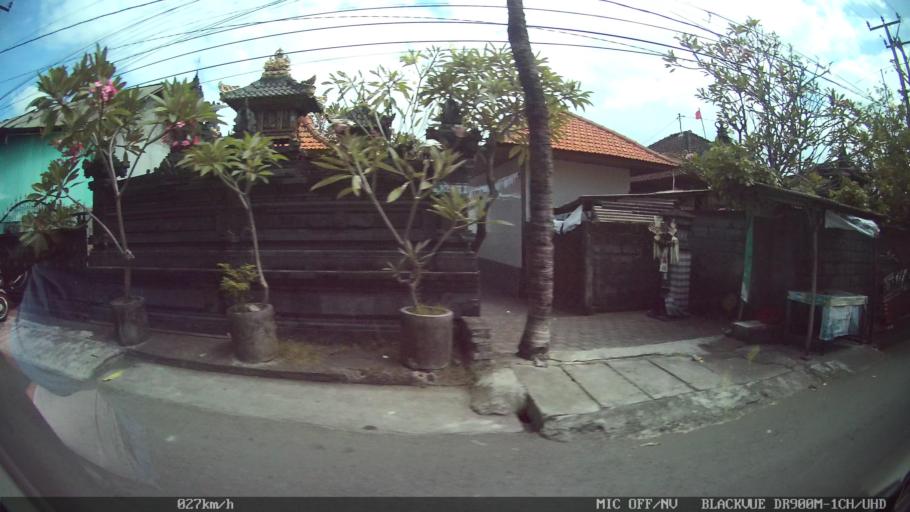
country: ID
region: Bali
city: Karyadharma
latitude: -8.6804
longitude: 115.1842
